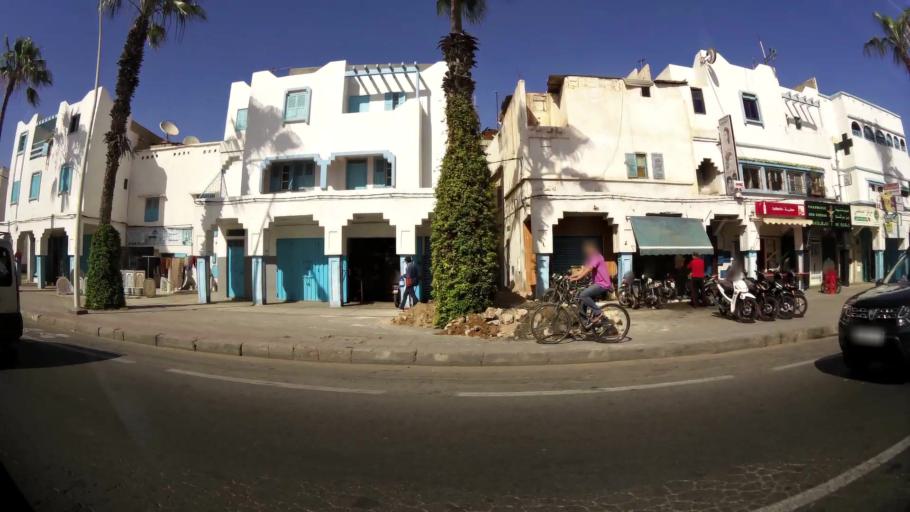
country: MA
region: Oued ed Dahab-Lagouira
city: Dakhla
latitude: 30.3851
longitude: -9.5716
